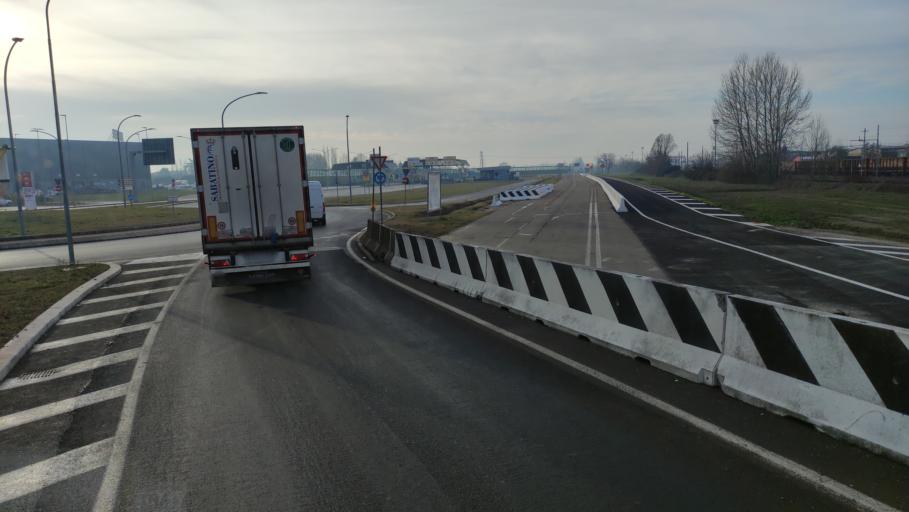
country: IT
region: Emilia-Romagna
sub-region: Provincia di Bologna
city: San Giorgio di Piano
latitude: 44.6122
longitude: 11.3747
